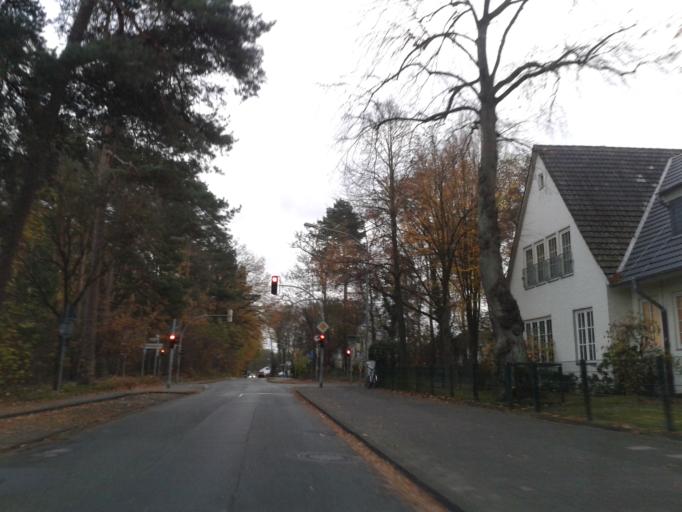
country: DE
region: North Rhine-Westphalia
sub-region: Regierungsbezirk Detmold
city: Paderborn
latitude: 51.7522
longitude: 8.7356
